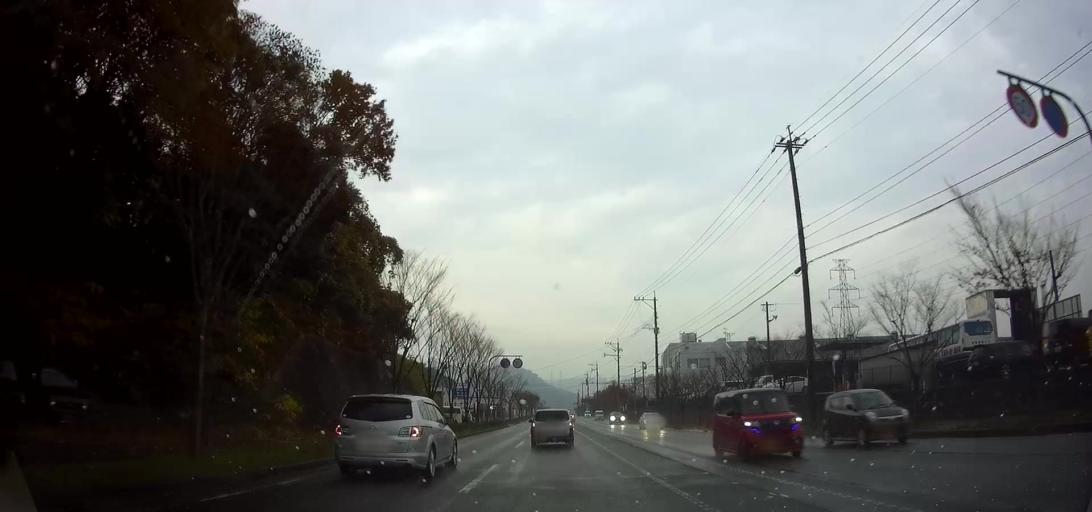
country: JP
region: Nagasaki
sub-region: Isahaya-shi
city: Isahaya
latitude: 32.8421
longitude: 130.0131
